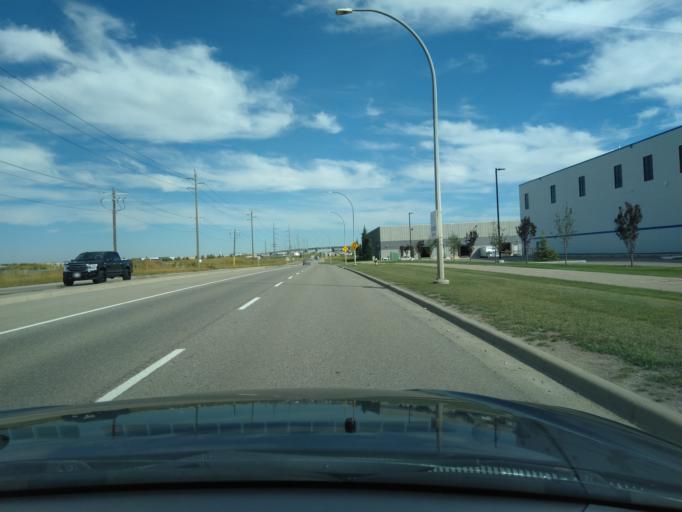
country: CA
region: Alberta
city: Calgary
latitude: 51.0959
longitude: -113.9966
